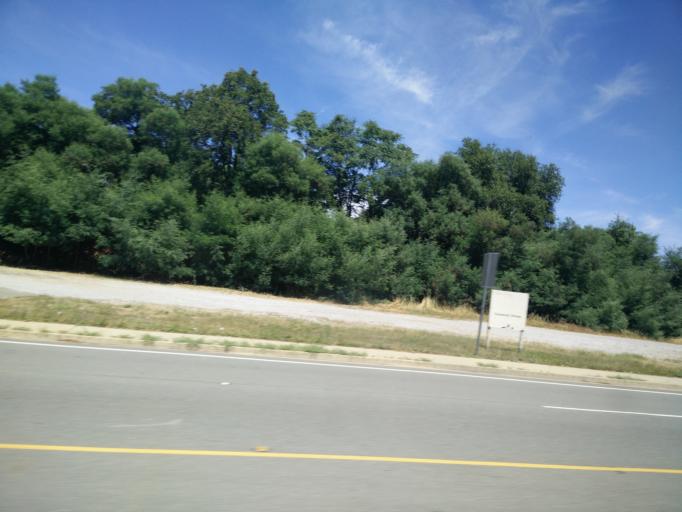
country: US
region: California
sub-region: Shasta County
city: Shasta Lake
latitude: 40.6802
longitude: -122.3533
